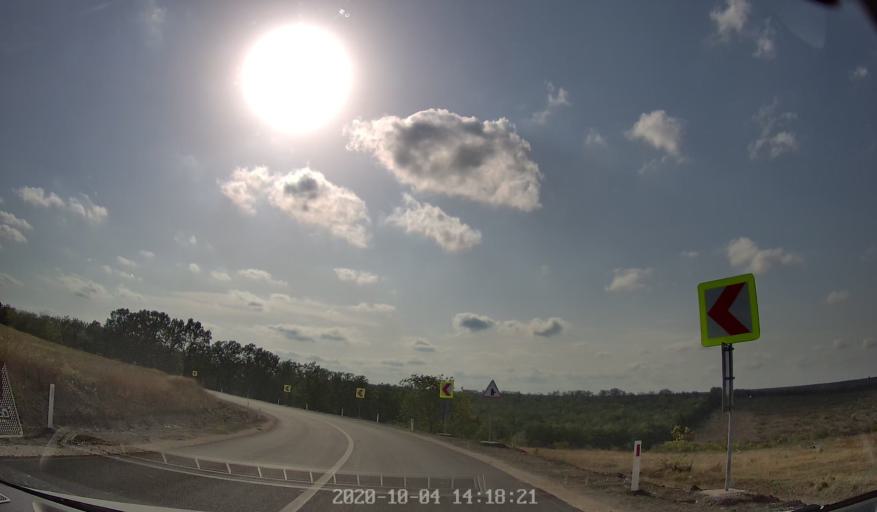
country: MD
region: Rezina
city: Saharna
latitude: 47.6000
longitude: 28.9759
